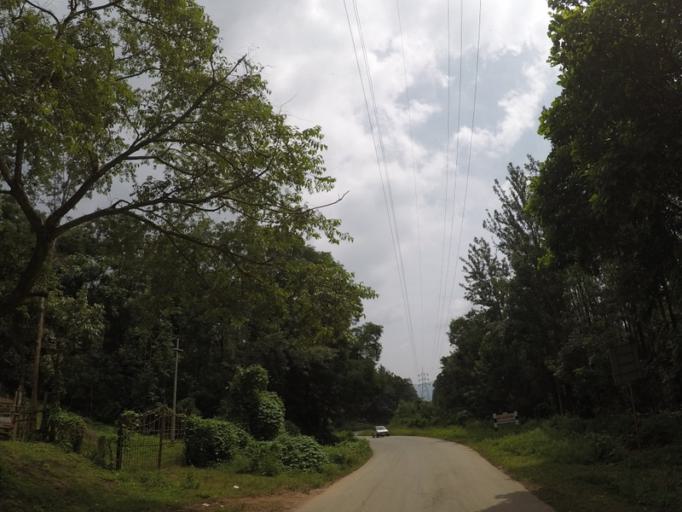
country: IN
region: Karnataka
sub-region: Chikmagalur
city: Chikmagalur
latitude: 13.4507
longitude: 75.8017
